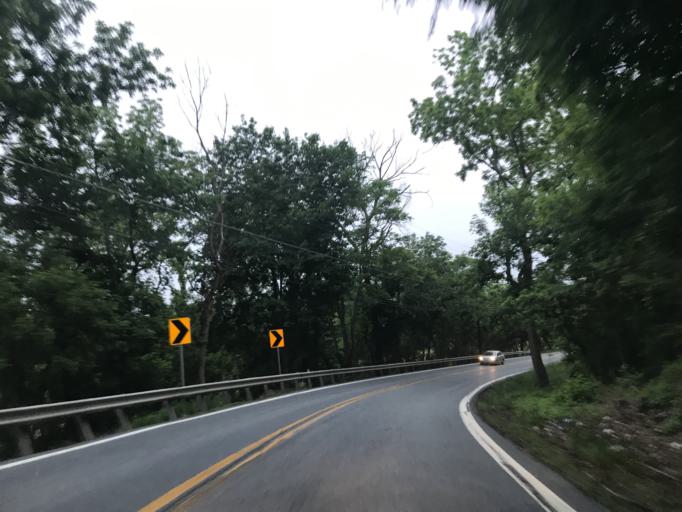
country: US
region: Maryland
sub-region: Frederick County
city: Linganore
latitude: 39.4824
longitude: -77.2403
